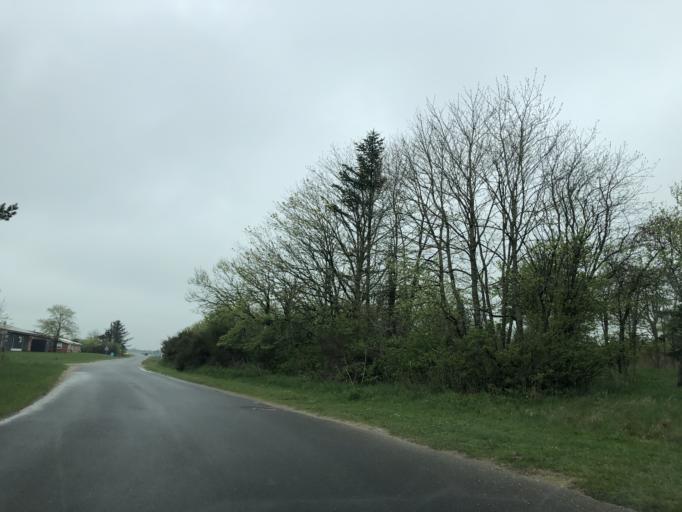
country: DK
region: Central Jutland
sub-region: Lemvig Kommune
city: Lemvig
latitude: 56.5135
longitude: 8.3116
